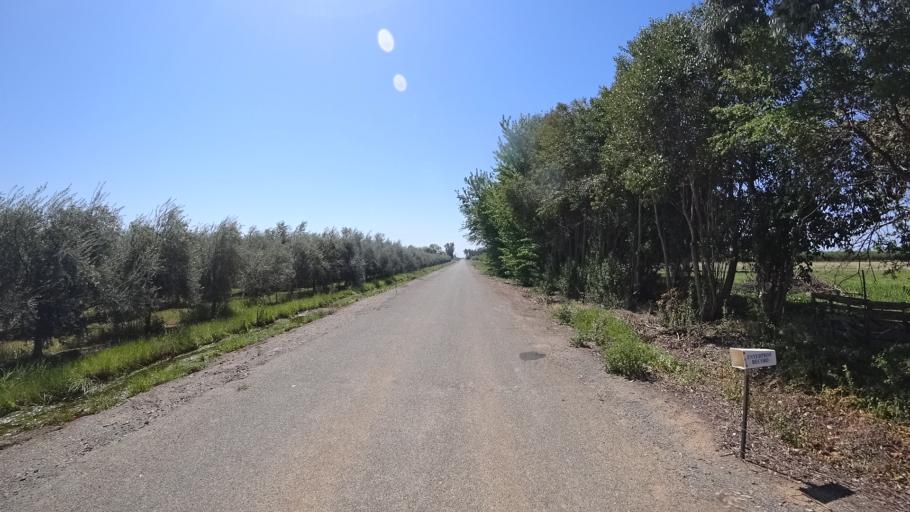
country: US
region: California
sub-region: Glenn County
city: Orland
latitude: 39.7972
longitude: -122.1691
